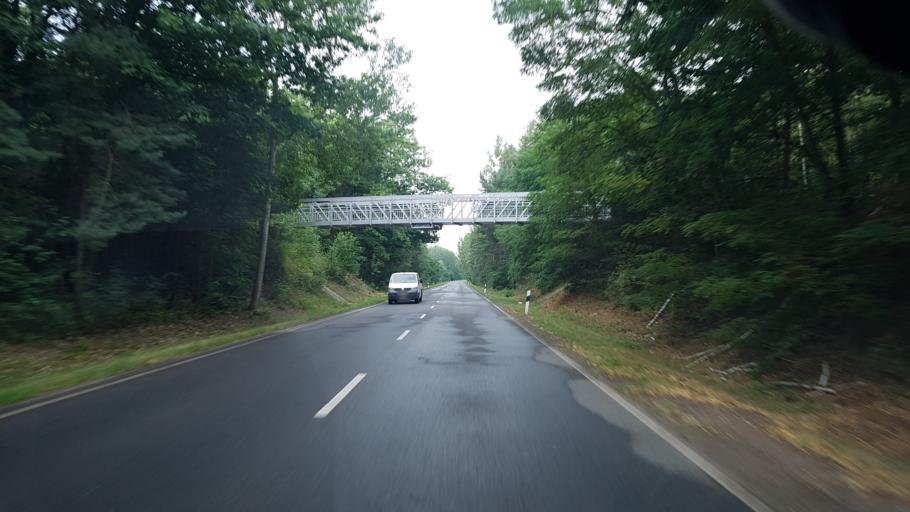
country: DE
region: Brandenburg
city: Lauchhammer
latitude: 51.5033
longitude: 13.7425
